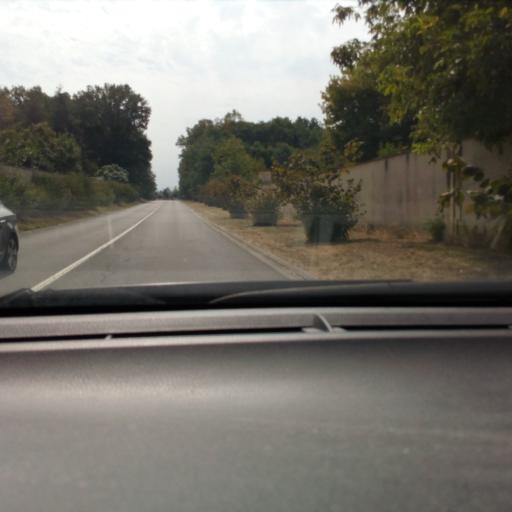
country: FR
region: Poitou-Charentes
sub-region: Departement de la Charente
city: Fleac
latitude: 45.6760
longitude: 0.0989
